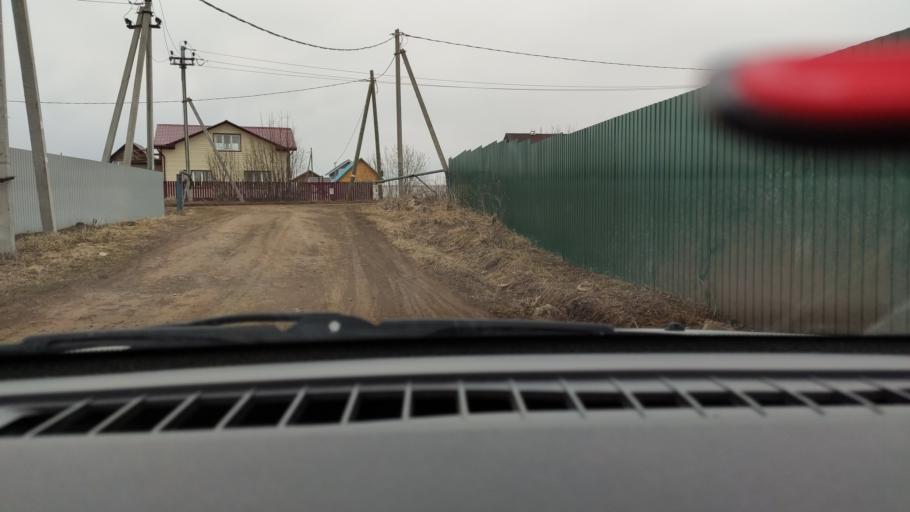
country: RU
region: Perm
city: Kultayevo
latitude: 57.8961
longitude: 56.0151
